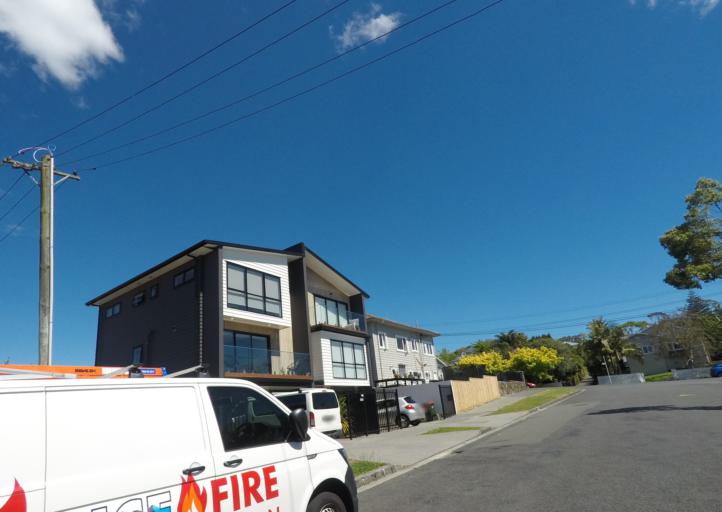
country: NZ
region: Auckland
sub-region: Auckland
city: Auckland
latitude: -36.8703
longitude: 174.7310
